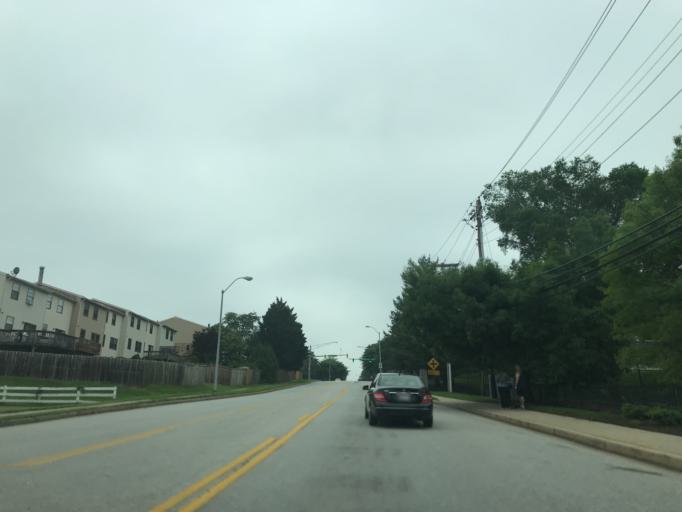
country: US
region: Maryland
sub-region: Baltimore County
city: Charlestown
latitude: 39.2654
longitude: -76.7011
